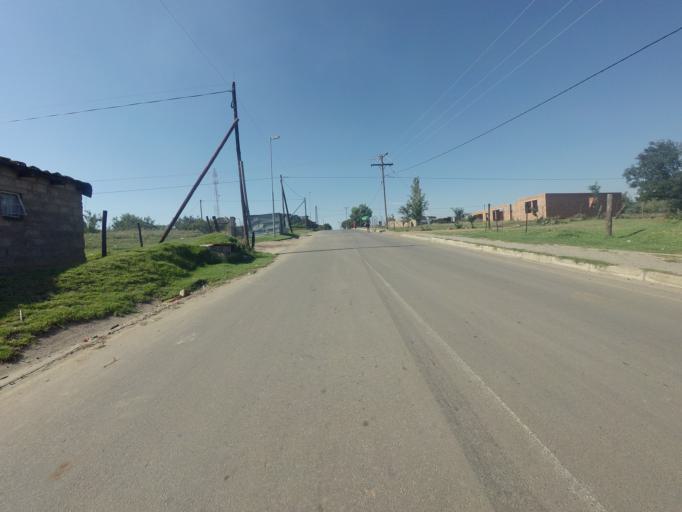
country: LS
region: Berea
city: Teyateyaneng
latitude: -29.1371
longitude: 27.7506
